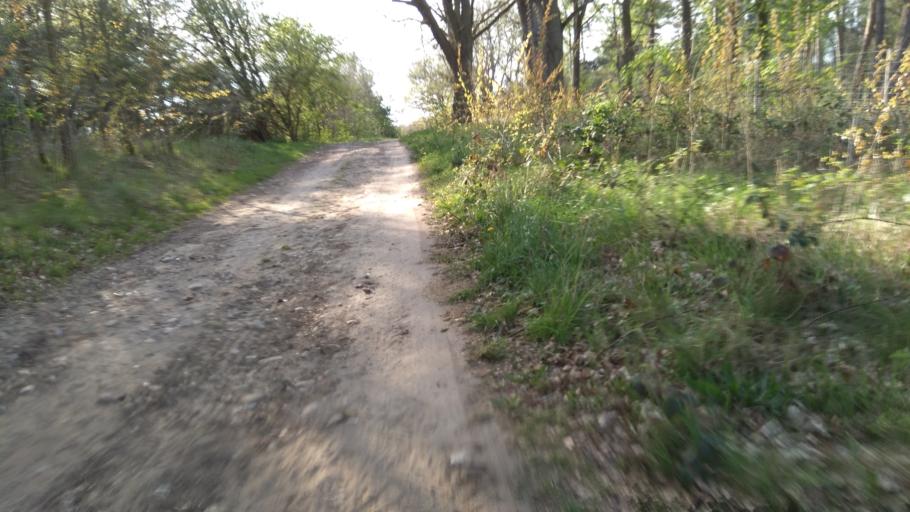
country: DE
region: Lower Saxony
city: Buxtehude
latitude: 53.4391
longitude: 9.6666
